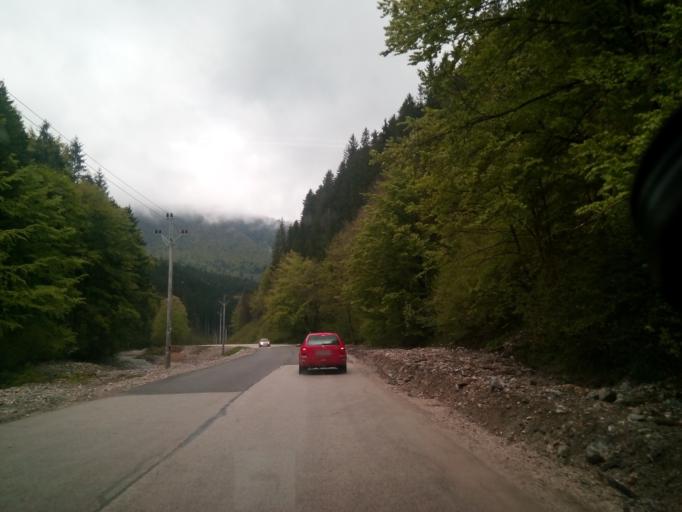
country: SK
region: Zilinsky
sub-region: Okres Zilina
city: Terchova
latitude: 49.2173
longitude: 19.0359
